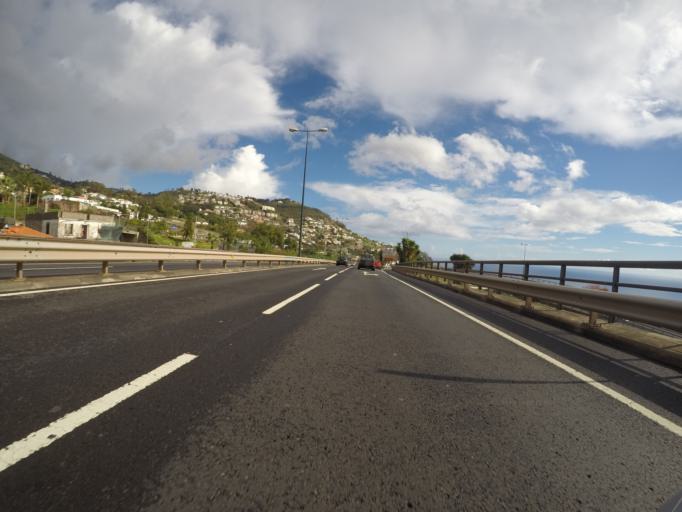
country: PT
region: Madeira
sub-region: Funchal
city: Nossa Senhora do Monte
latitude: 32.6574
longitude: -16.8864
